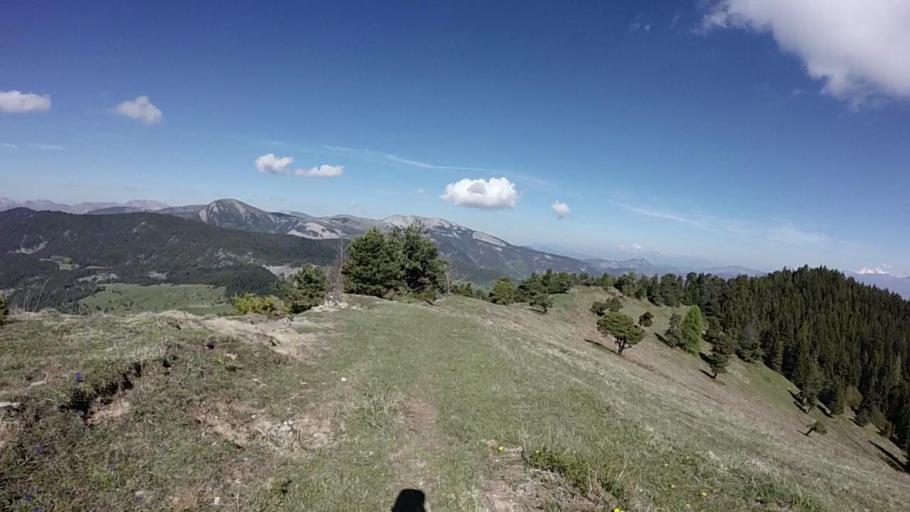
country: FR
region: Provence-Alpes-Cote d'Azur
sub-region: Departement des Alpes-de-Haute-Provence
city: Seyne-les-Alpes
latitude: 44.3195
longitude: 6.3740
